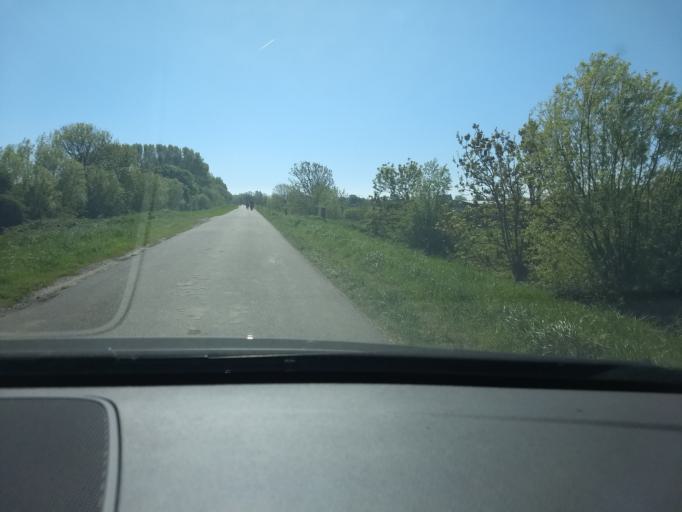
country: NL
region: Zeeland
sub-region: Gemeente Veere
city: Veere
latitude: 51.5812
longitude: 3.6122
